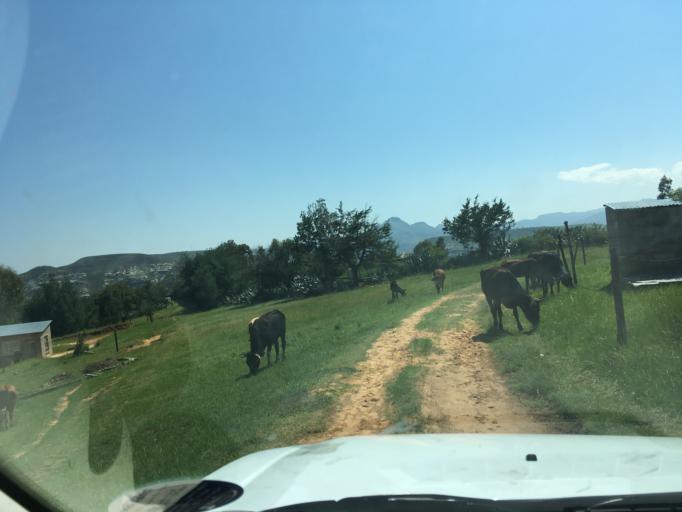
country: LS
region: Butha-Buthe
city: Butha-Buthe
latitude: -28.7253
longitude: 28.3658
